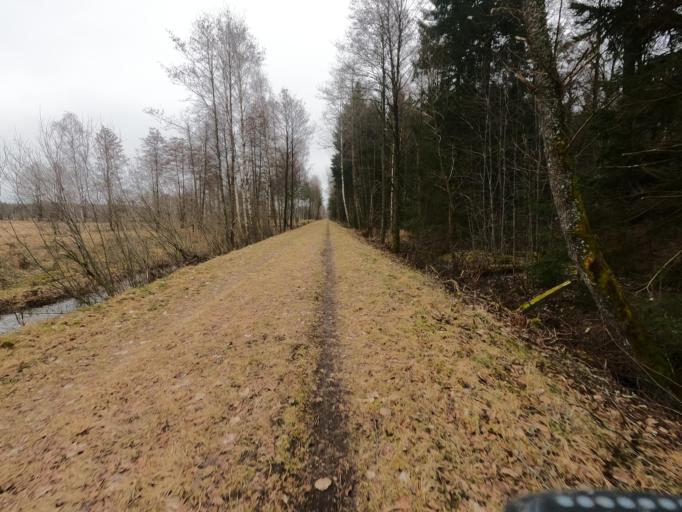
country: SE
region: Kronoberg
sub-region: Ljungby Kommun
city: Ljungby
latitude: 56.8253
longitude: 13.7461
